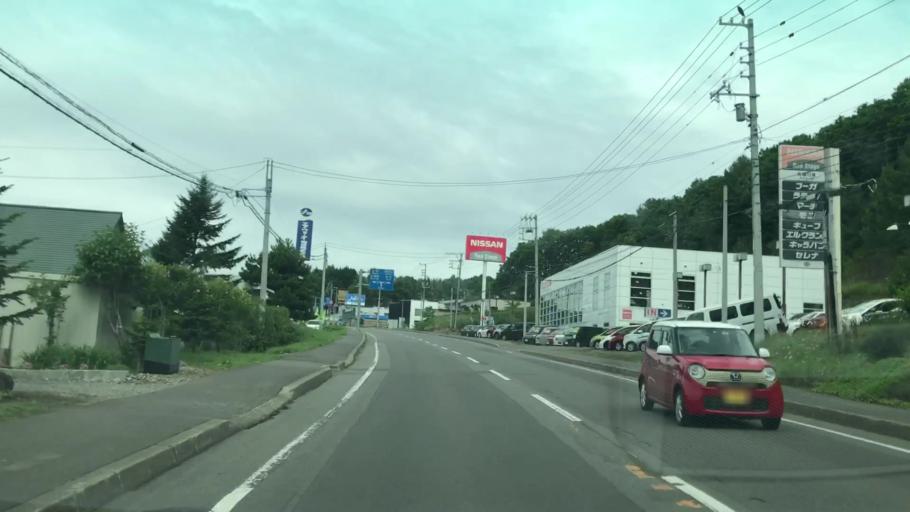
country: JP
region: Hokkaido
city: Otaru
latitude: 43.2171
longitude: 140.9571
